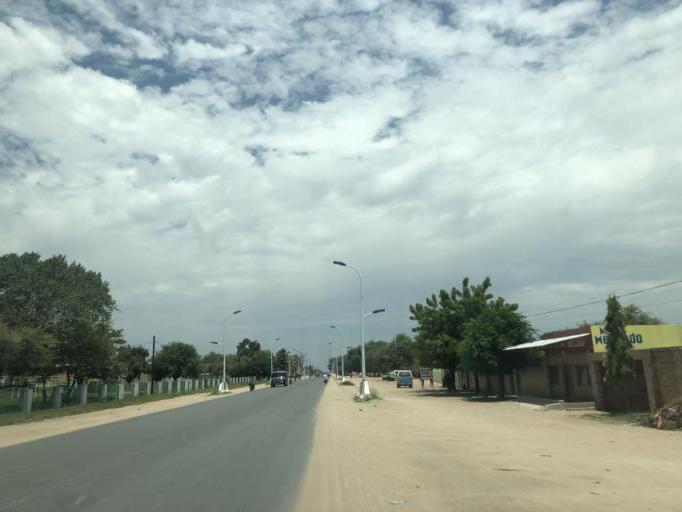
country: AO
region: Cunene
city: Ondjiva
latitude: -17.0800
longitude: 15.7374
